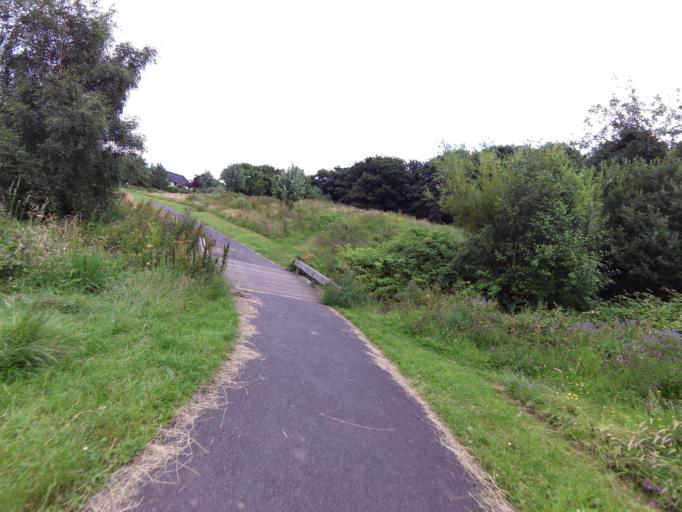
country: GB
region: Scotland
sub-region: East Lothian
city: Musselburgh
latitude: 55.9450
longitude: -3.0822
